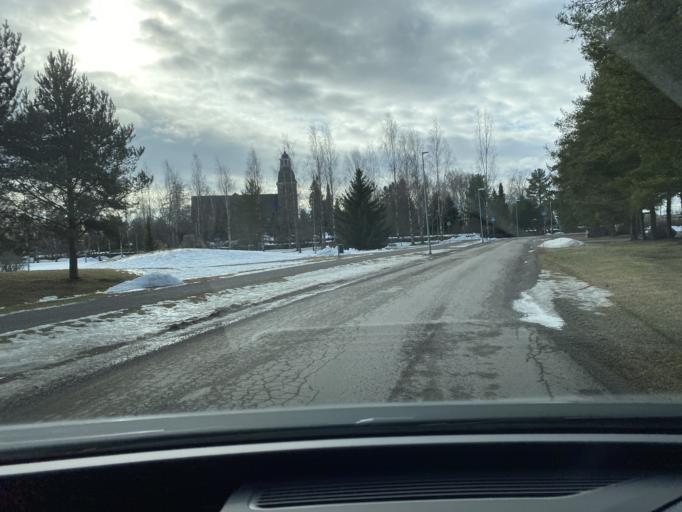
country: FI
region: Satakunta
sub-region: Pori
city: Huittinen
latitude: 61.1829
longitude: 22.6926
